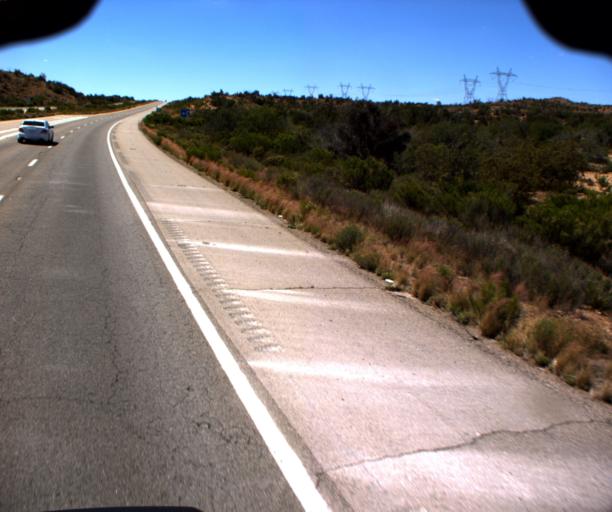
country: US
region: Arizona
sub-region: Yavapai County
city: Bagdad
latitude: 34.4673
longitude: -113.3094
